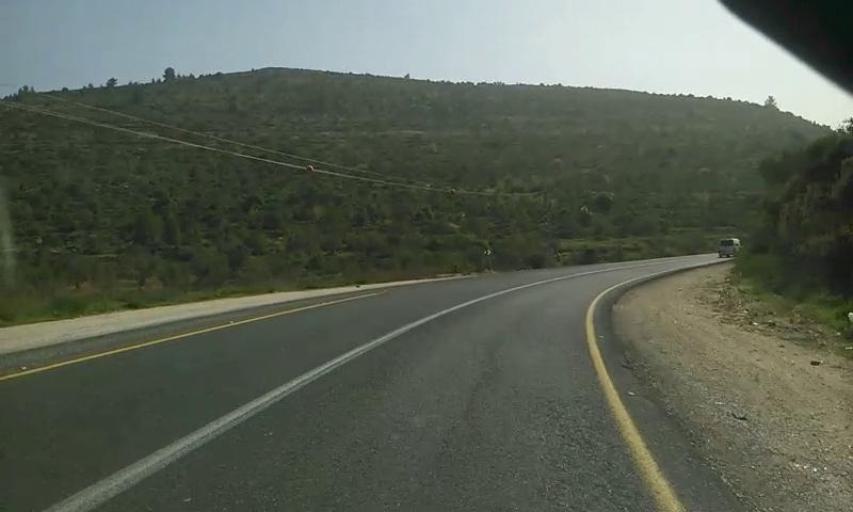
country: PS
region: West Bank
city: Silwad
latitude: 31.9985
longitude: 35.2395
